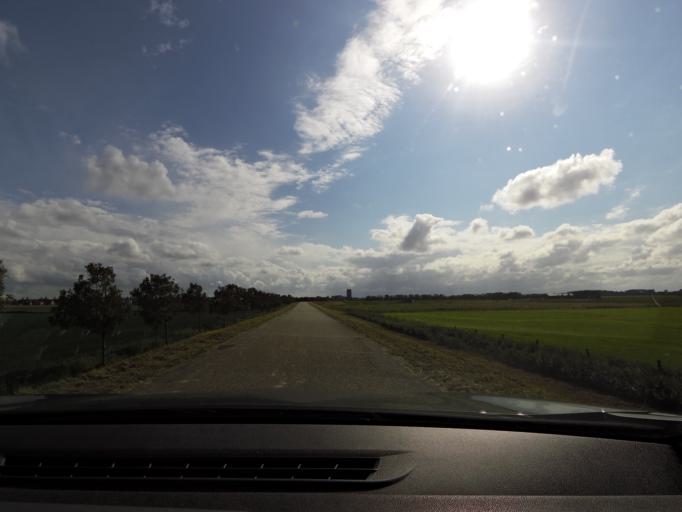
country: NL
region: South Holland
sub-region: Gemeente Goeree-Overflakkee
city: Goedereede
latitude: 51.8263
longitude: 3.9880
